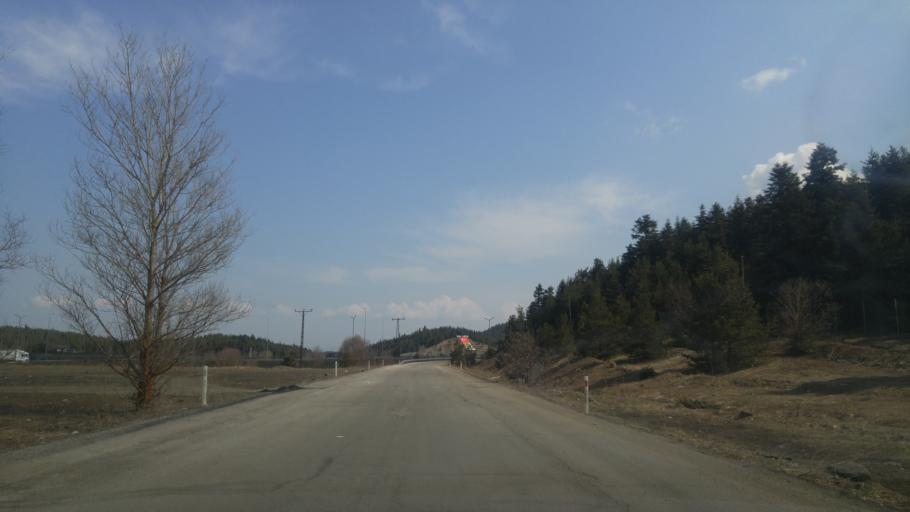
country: TR
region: Ankara
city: Pecenek
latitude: 40.6098
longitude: 32.2545
